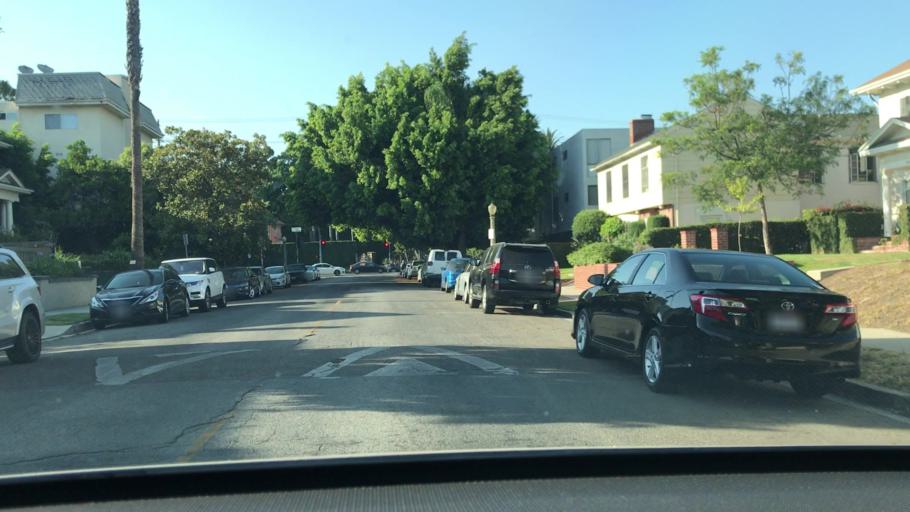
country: US
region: California
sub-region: Los Angeles County
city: Hollywood
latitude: 34.0679
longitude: -118.3173
